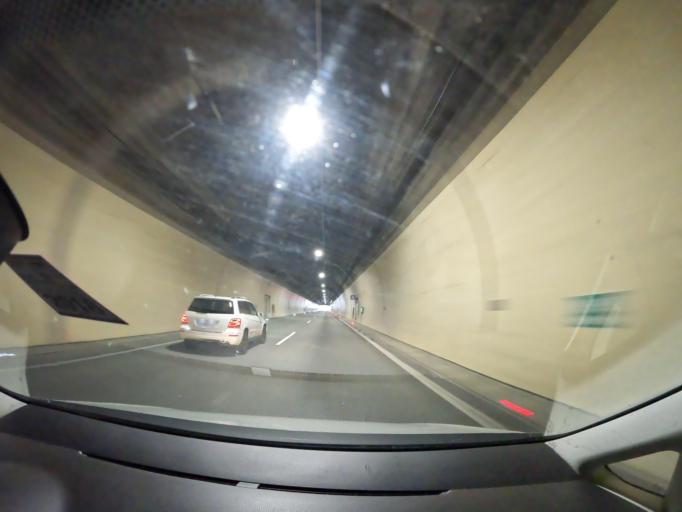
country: AT
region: Carinthia
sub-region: Politischer Bezirk Wolfsberg
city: Bad Sankt Leonhard im Lavanttal
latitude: 46.9125
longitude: 14.8250
